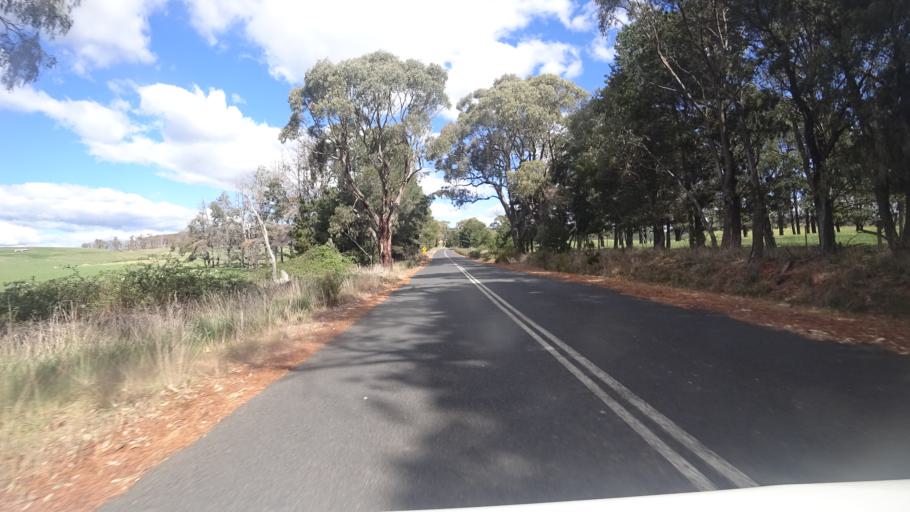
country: AU
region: New South Wales
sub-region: Oberon
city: Oberon
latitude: -33.6783
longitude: 149.7859
